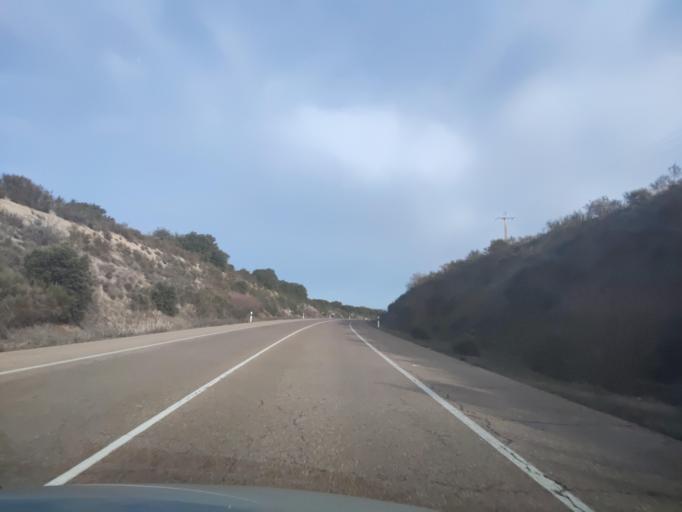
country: ES
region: Castille and Leon
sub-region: Provincia de Salamanca
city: Espeja
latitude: 40.5936
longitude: -6.6967
